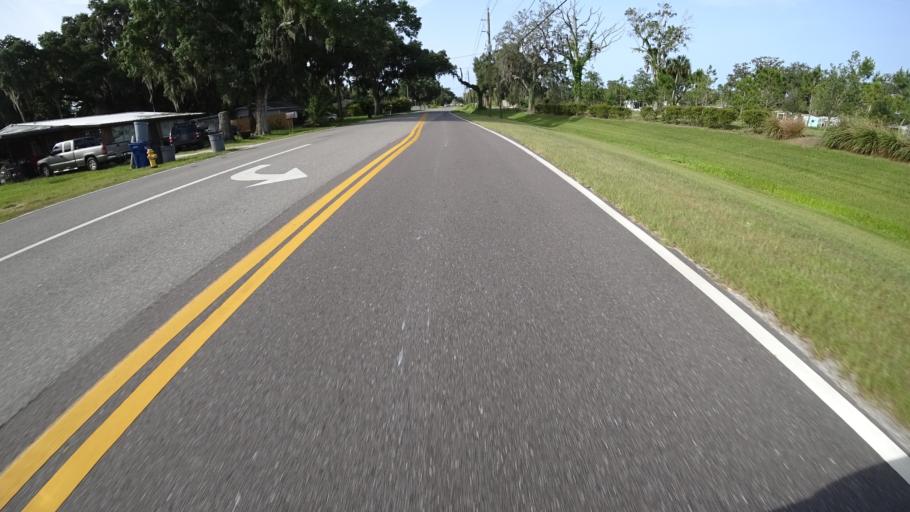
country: US
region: Florida
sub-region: Manatee County
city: Ellenton
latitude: 27.5405
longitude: -82.4914
